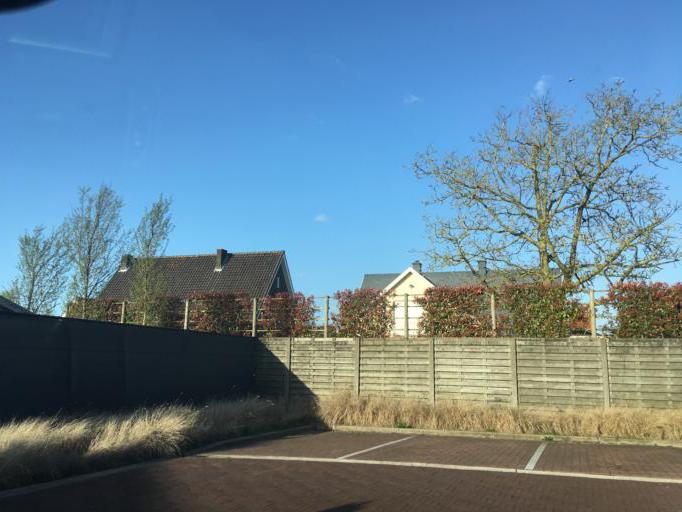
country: BE
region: Flanders
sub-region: Provincie West-Vlaanderen
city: Staden
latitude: 50.9726
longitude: 3.0193
